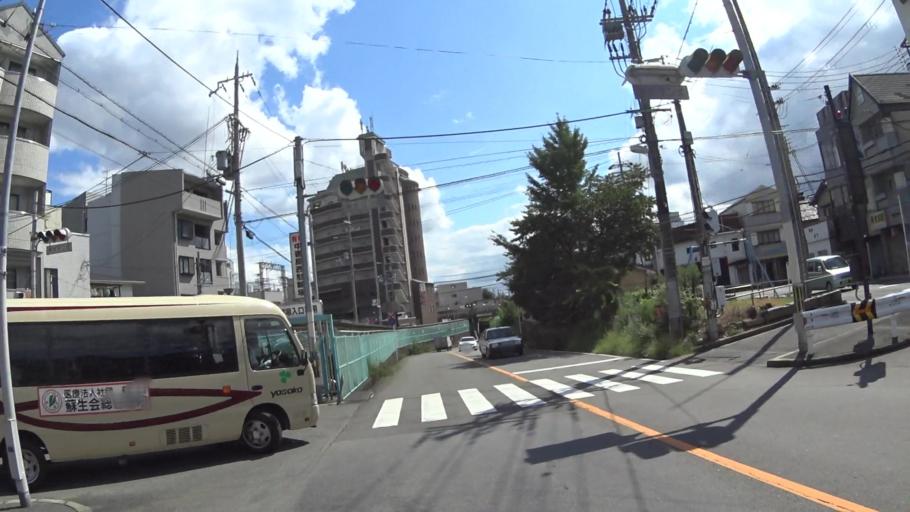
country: JP
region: Kyoto
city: Uji
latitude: 34.9277
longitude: 135.7589
